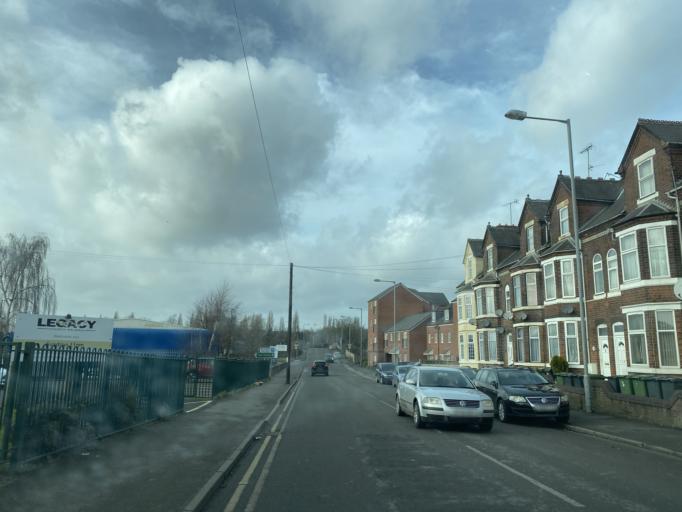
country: GB
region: England
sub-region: Walsall
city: Walsall
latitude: 52.5783
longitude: -1.9886
